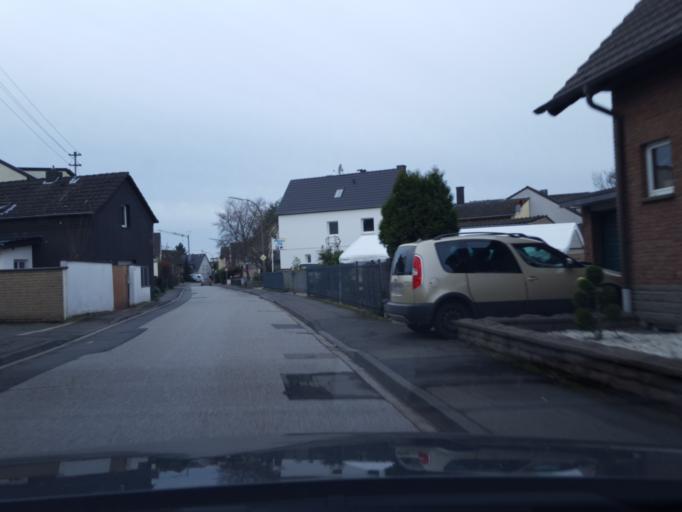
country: DE
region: North Rhine-Westphalia
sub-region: Regierungsbezirk Koln
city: Bonn
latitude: 50.7762
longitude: 7.0690
